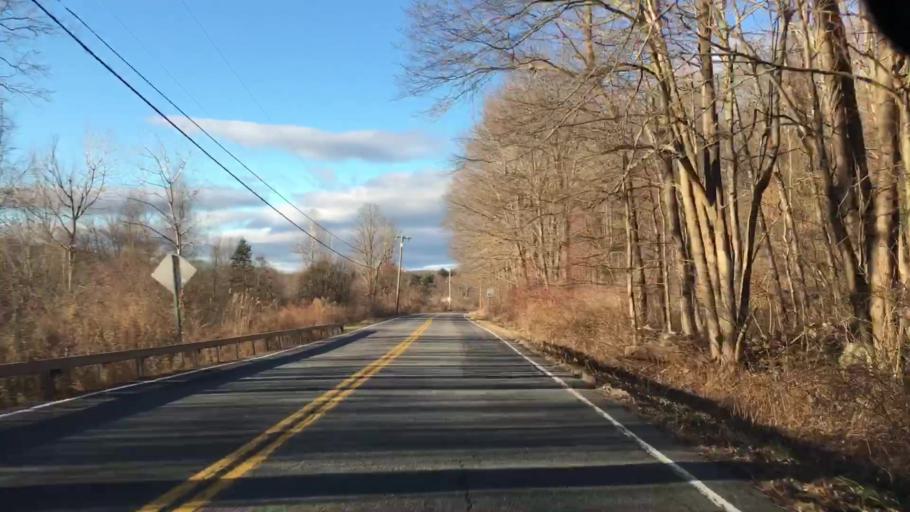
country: US
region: New York
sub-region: Putnam County
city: Lake Carmel
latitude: 41.4912
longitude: -73.6615
